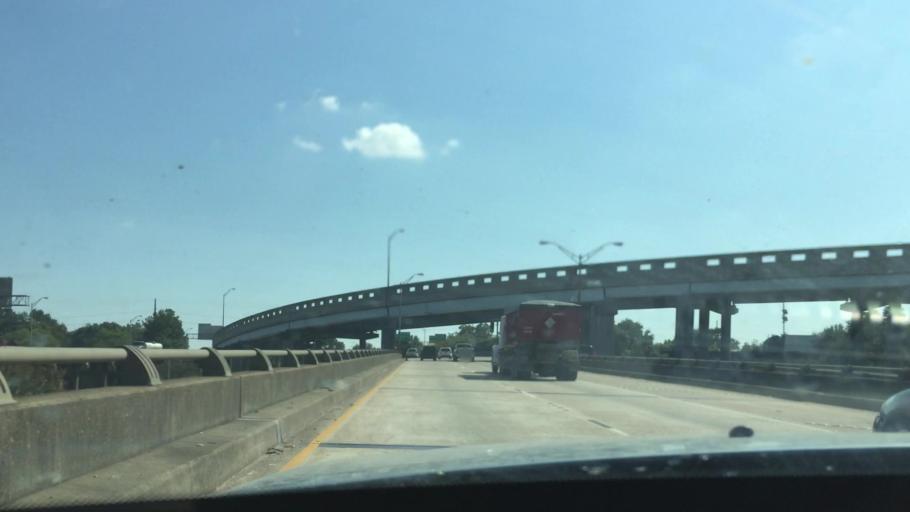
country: US
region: Louisiana
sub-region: East Baton Rouge Parish
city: Baton Rouge
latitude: 30.4398
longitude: -91.1784
